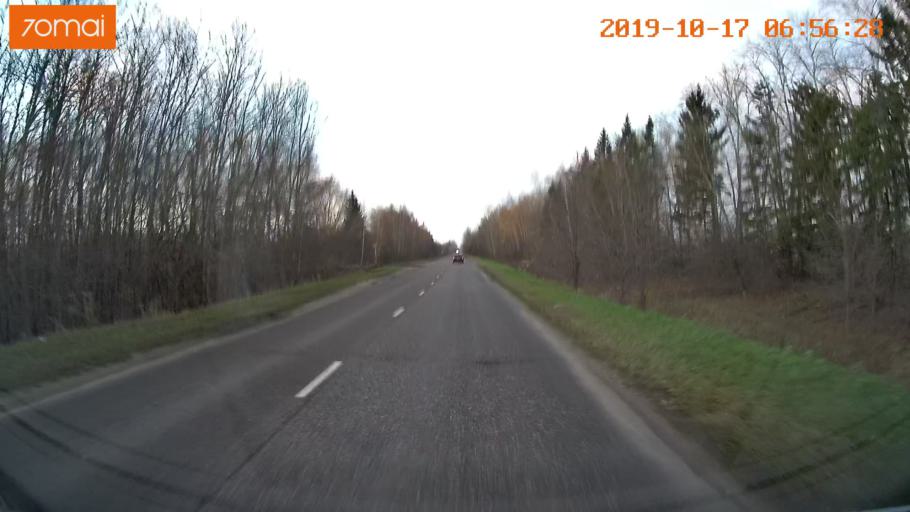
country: RU
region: Vladimir
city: Suzdal'
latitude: 56.4463
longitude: 40.4475
